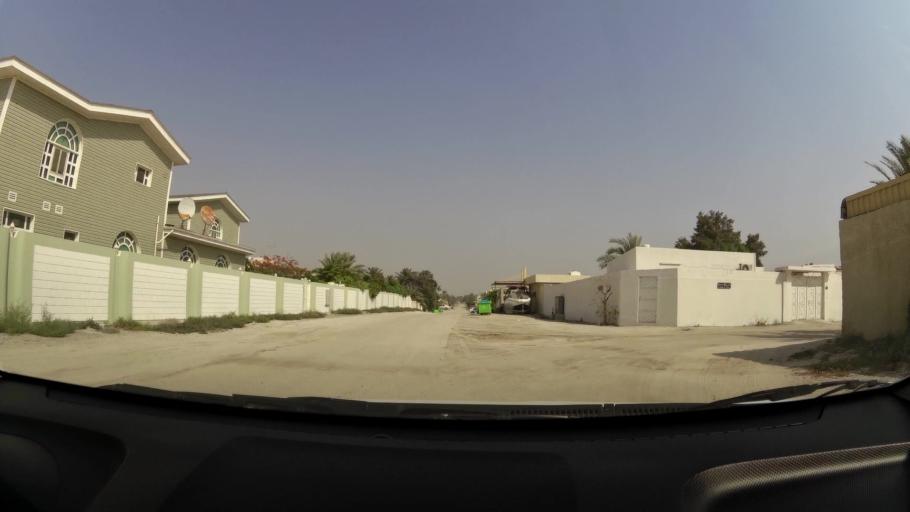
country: AE
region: Ajman
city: Ajman
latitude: 25.3918
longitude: 55.4278
